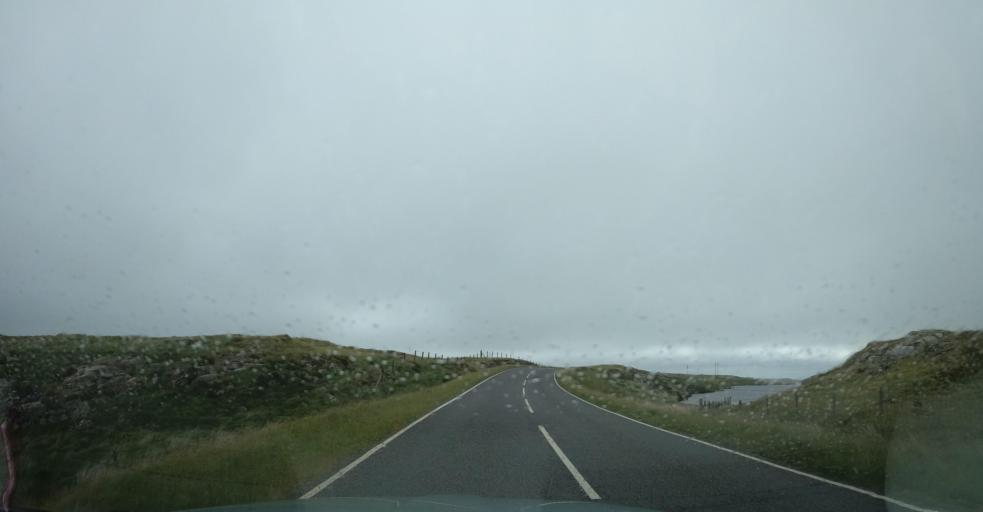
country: GB
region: Scotland
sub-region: Eilean Siar
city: Isle of North Uist
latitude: 57.5971
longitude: -7.1903
